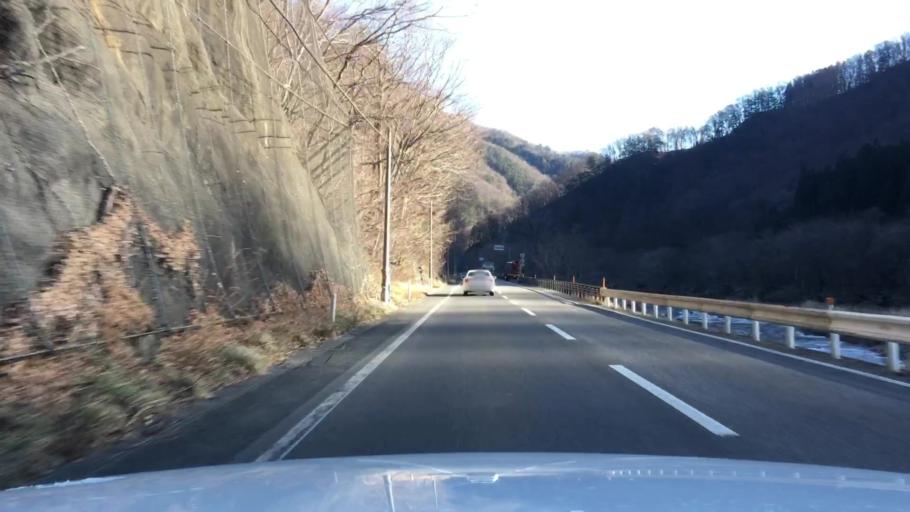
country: JP
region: Iwate
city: Miyako
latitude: 39.5975
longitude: 141.7235
